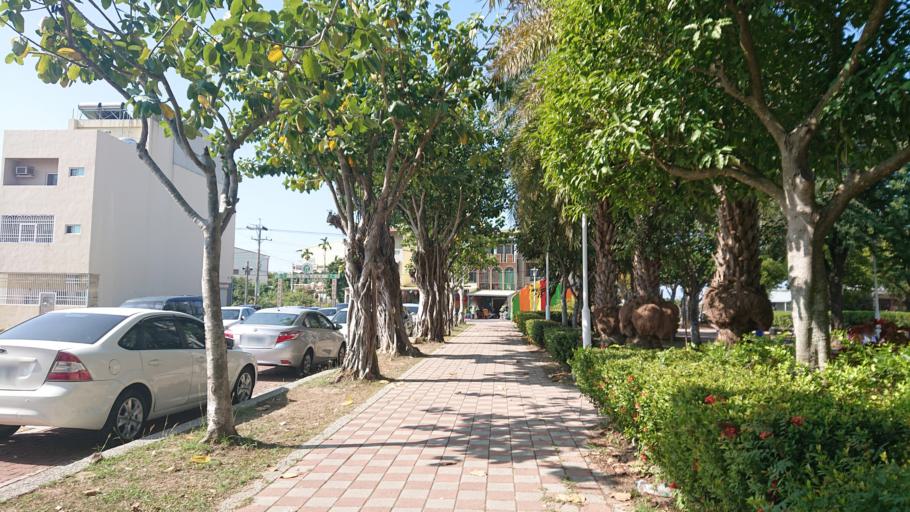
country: TW
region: Taiwan
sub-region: Tainan
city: Tainan
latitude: 23.0659
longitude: 120.1272
